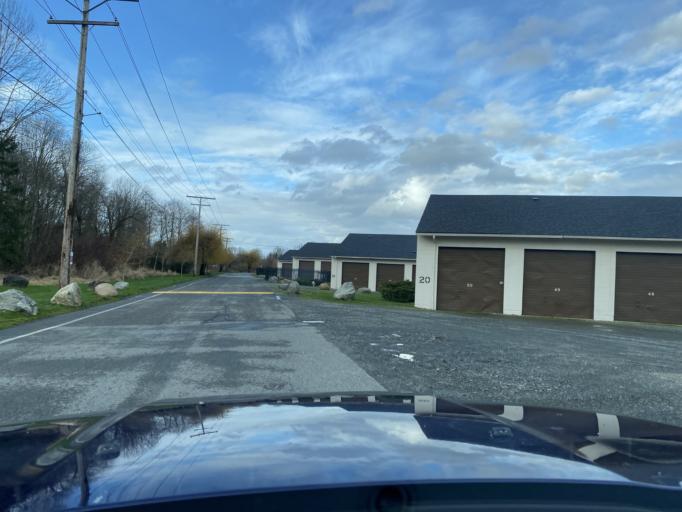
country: US
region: Washington
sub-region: King County
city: Issaquah
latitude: 47.5469
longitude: -122.0671
